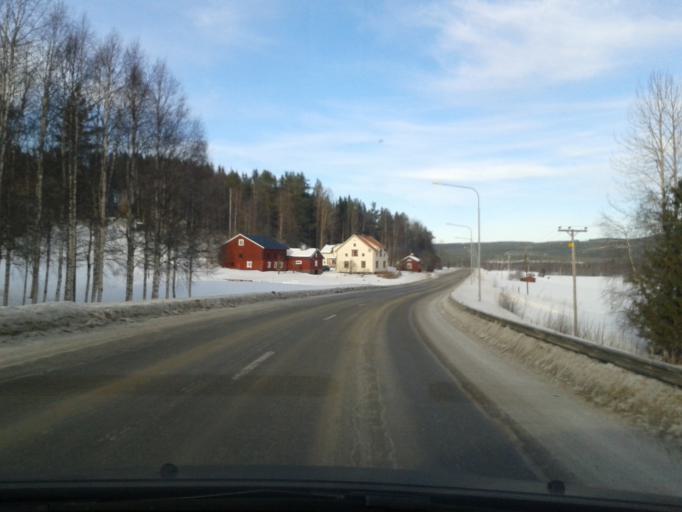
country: SE
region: Vaesternorrland
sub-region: OErnskoeldsviks Kommun
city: Bredbyn
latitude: 63.4929
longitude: 18.0801
